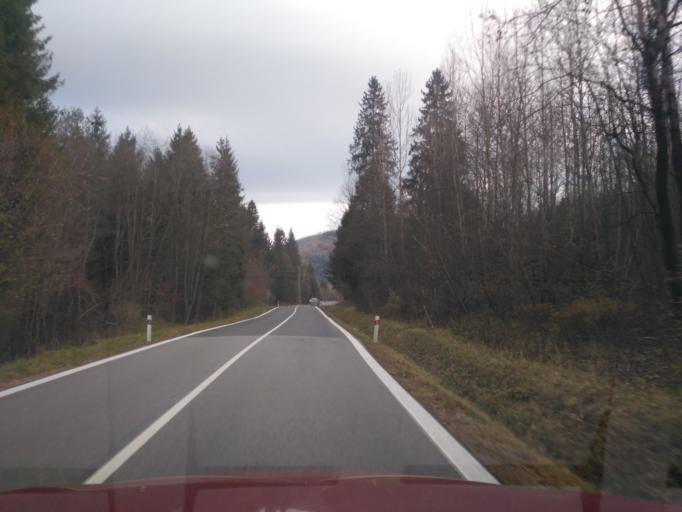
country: SK
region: Kosicky
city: Spisska Nova Ves
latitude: 48.8167
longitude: 20.6647
